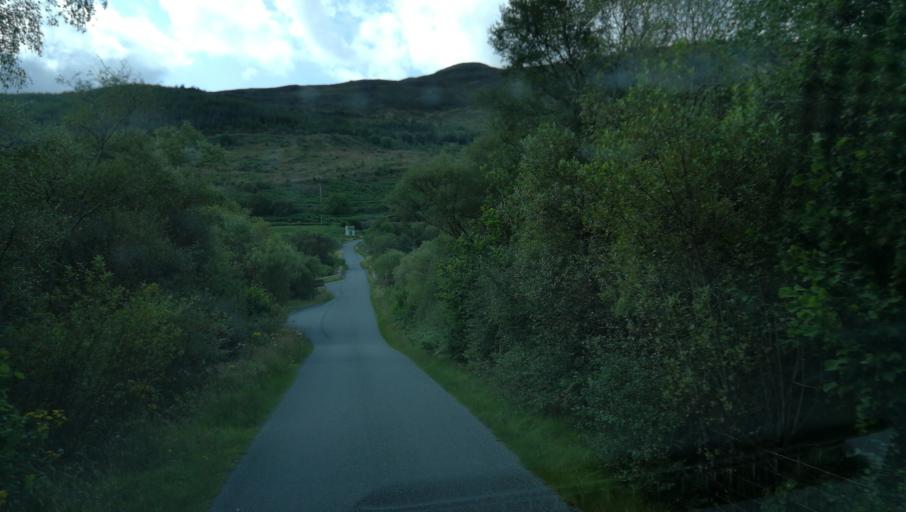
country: GB
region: Scotland
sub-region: Highland
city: Portree
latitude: 57.3872
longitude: -6.1990
